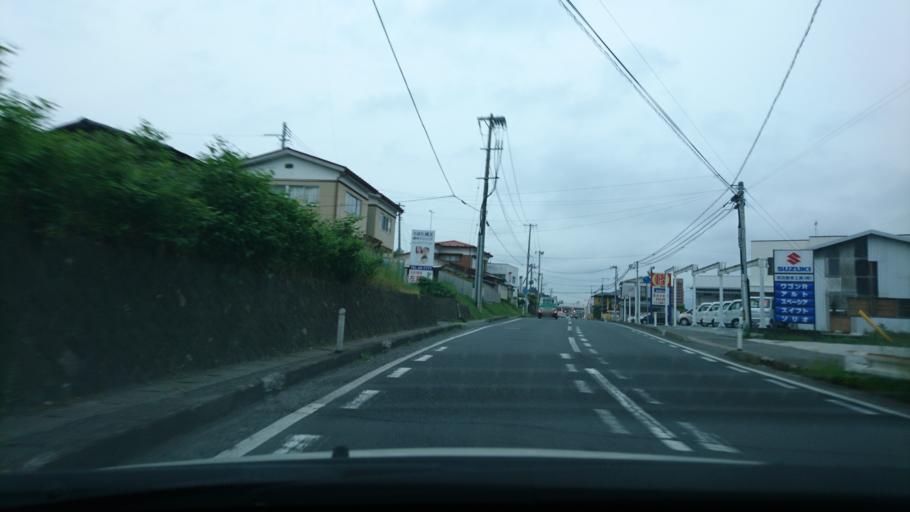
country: JP
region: Iwate
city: Ichinoseki
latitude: 38.9137
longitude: 141.1315
